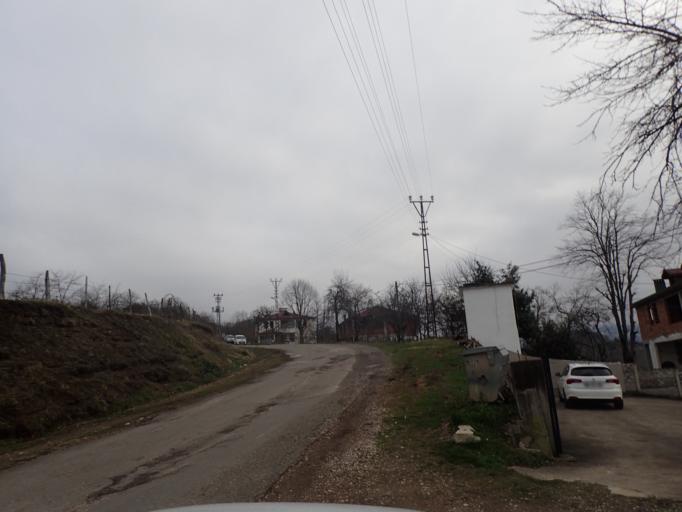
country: TR
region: Ordu
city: Camas
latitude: 40.9268
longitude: 37.5191
